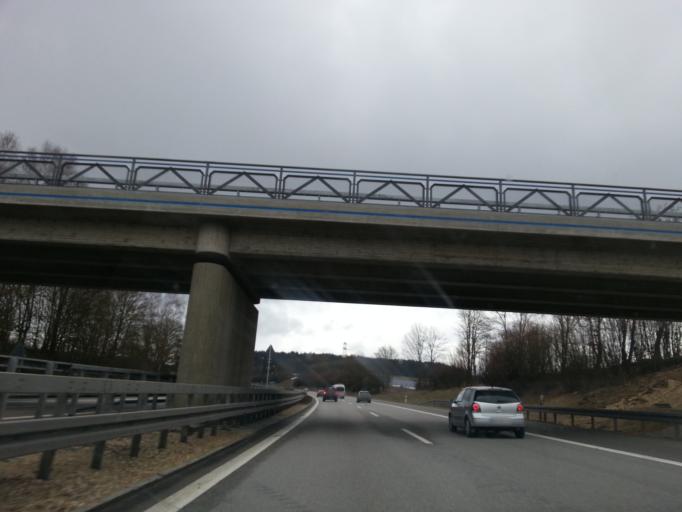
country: DE
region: Bavaria
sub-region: Upper Palatinate
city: Hohenfels
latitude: 49.1614
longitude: 11.8389
